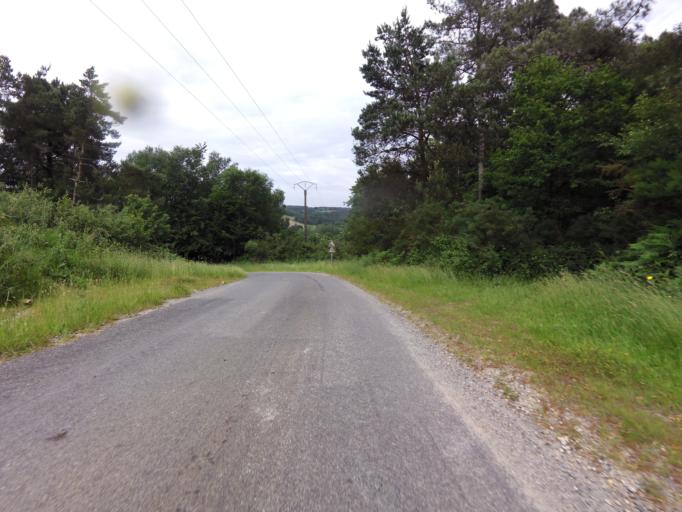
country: FR
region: Brittany
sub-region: Departement du Morbihan
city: Molac
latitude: 47.7173
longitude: -2.4709
